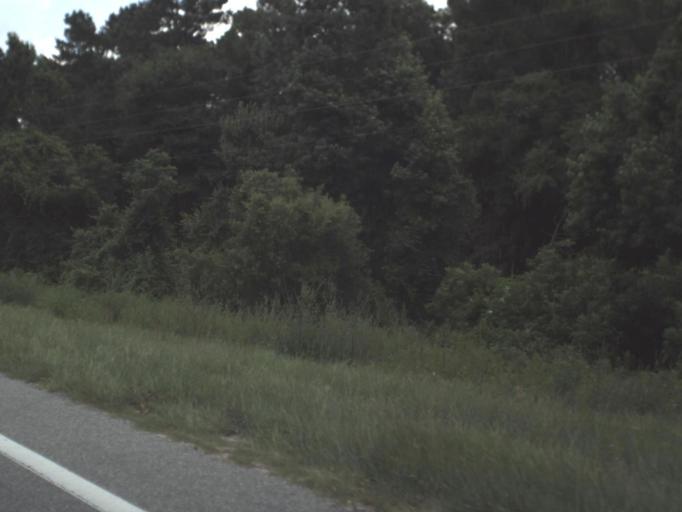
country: US
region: Florida
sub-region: Hamilton County
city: Jasper
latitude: 30.4955
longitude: -82.9325
